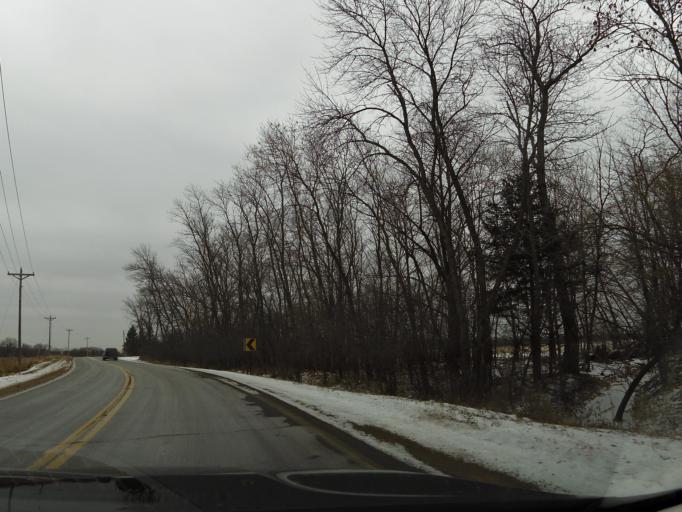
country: US
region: Minnesota
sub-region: Hennepin County
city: Medina
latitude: 45.0368
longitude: -93.5804
